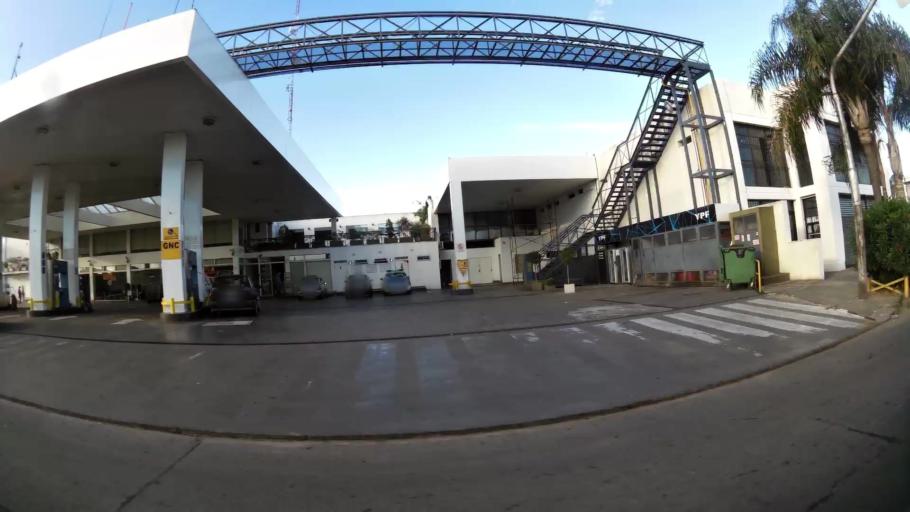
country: AR
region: Santa Fe
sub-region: Departamento de Rosario
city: Rosario
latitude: -32.9750
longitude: -60.6687
